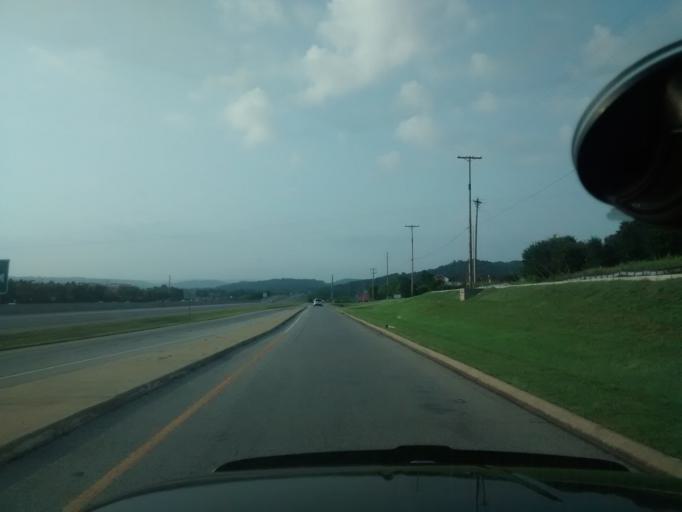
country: US
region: Arkansas
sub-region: Washington County
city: Fayetteville
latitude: 36.0609
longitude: -94.1987
